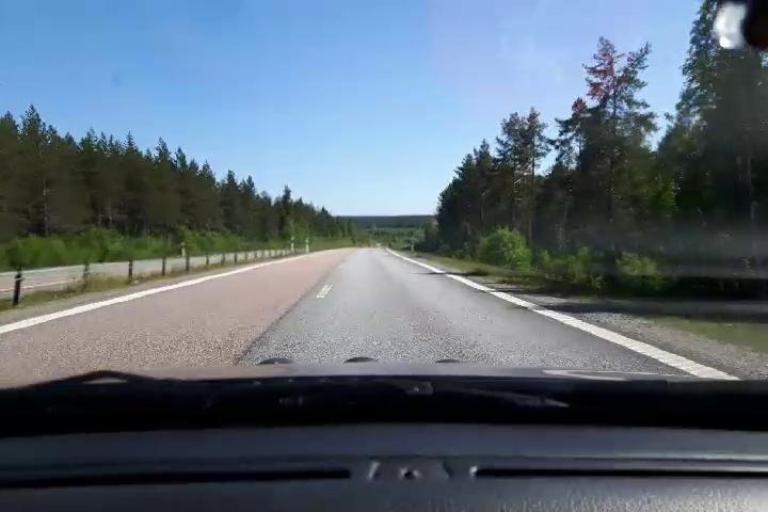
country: SE
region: Gaevleborg
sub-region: Soderhamns Kommun
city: Soderhamn
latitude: 61.3656
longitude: 17.0110
